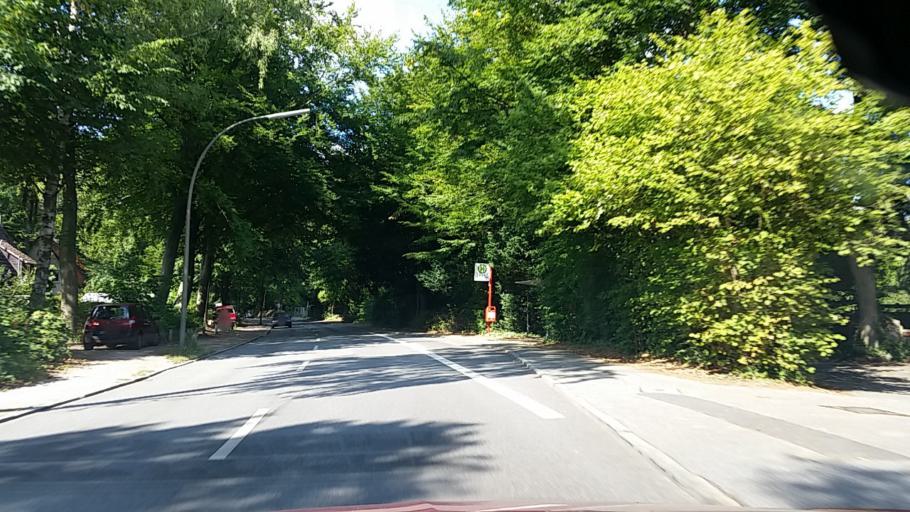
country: DE
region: Hamburg
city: Bergstedt
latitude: 53.6608
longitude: 10.1562
